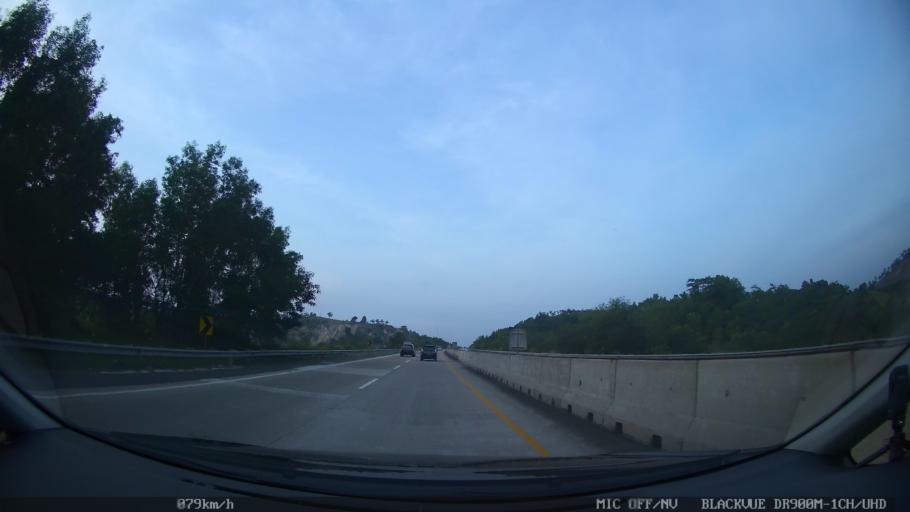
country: ID
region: Lampung
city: Penengahan
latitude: -5.8322
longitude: 105.7313
